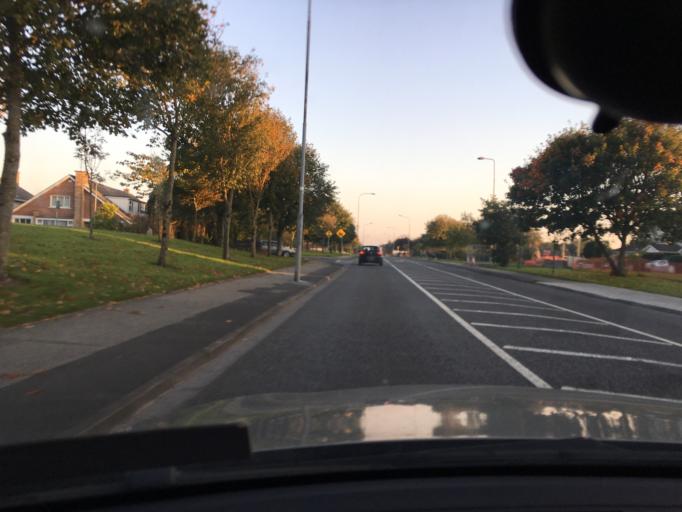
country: IE
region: Connaught
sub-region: County Galway
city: Gaillimh
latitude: 53.2845
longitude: -9.0735
